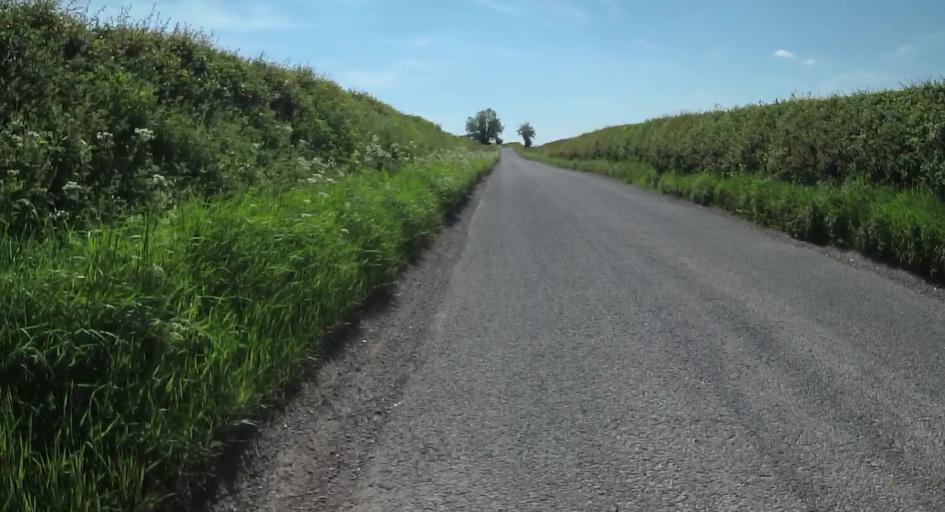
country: GB
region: England
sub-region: Hampshire
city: Four Marks
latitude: 51.1534
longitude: -1.1418
